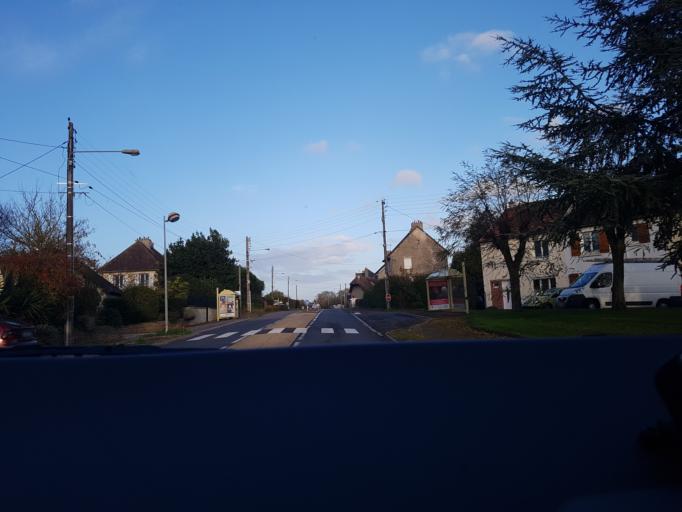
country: FR
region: Lower Normandy
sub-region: Departement du Calvados
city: Troarn
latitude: 49.1849
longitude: -0.1605
